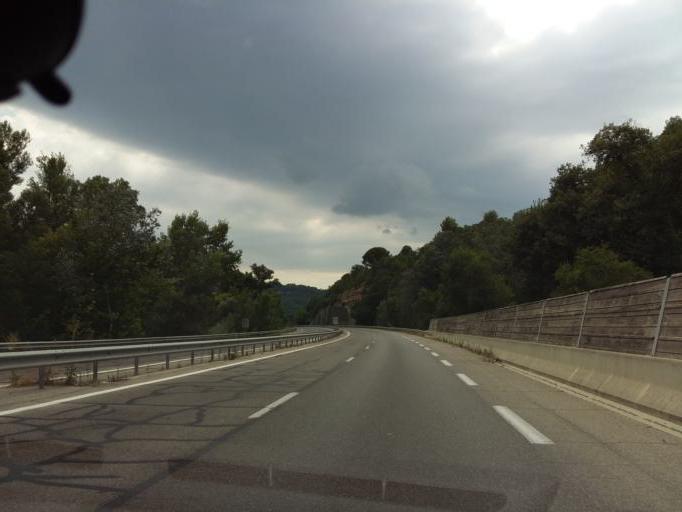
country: FR
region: Provence-Alpes-Cote d'Azur
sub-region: Departement du Vaucluse
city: Goult
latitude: 43.8572
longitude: 5.2599
